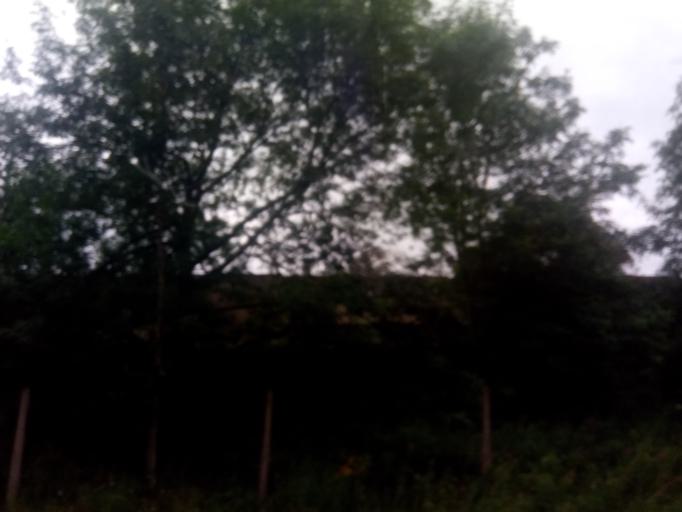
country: GB
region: England
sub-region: North Yorkshire
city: Settle
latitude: 54.0174
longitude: -2.2566
